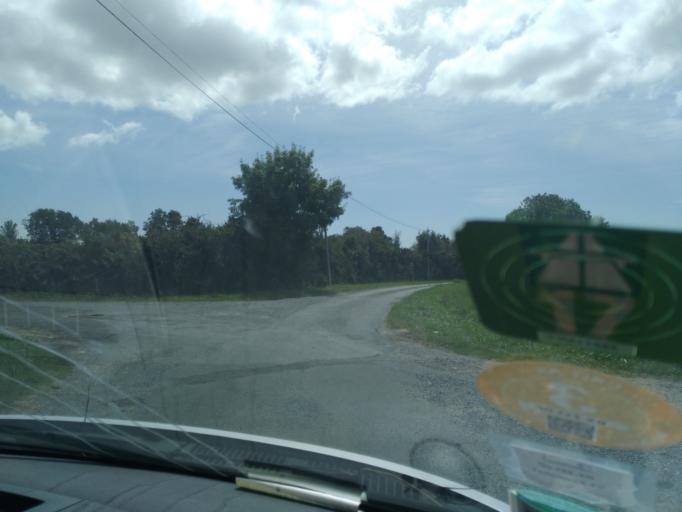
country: FR
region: Poitou-Charentes
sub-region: Departement de la Charente-Maritime
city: Chaillevette
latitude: 45.7133
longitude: -1.0774
